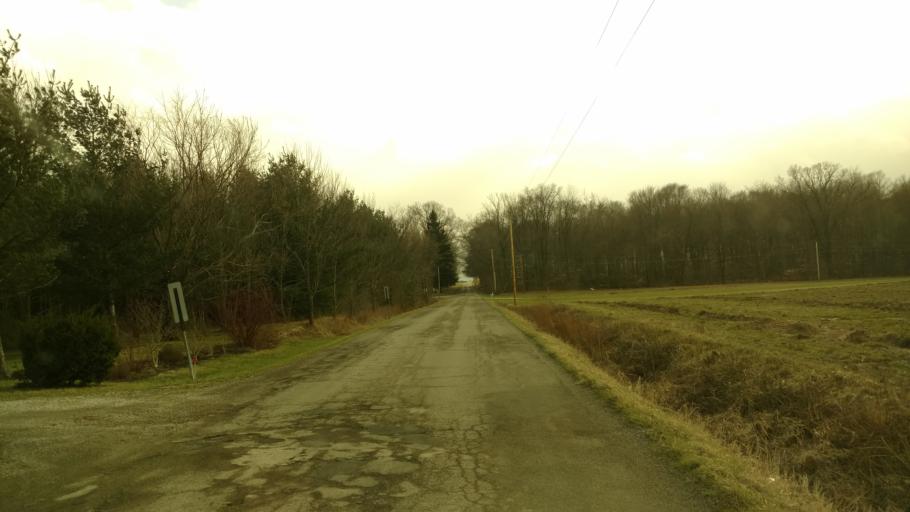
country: US
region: Ohio
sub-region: Crawford County
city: Galion
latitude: 40.6841
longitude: -82.7464
